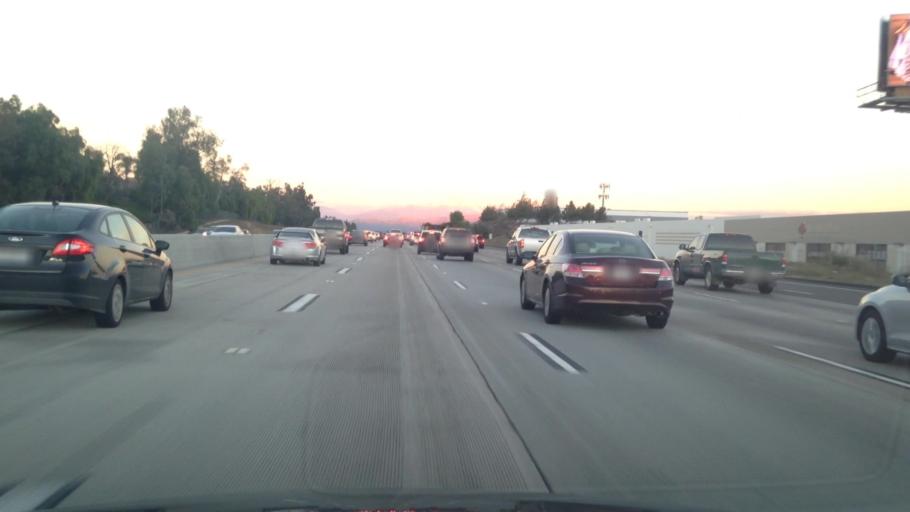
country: US
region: California
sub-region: Riverside County
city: Home Gardens
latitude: 33.8880
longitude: -117.5121
